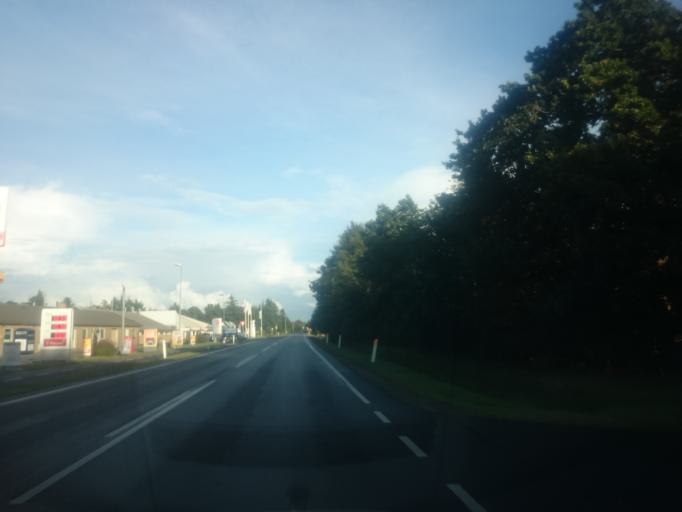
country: DK
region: South Denmark
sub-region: Billund Kommune
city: Billund
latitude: 55.7352
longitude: 9.1017
